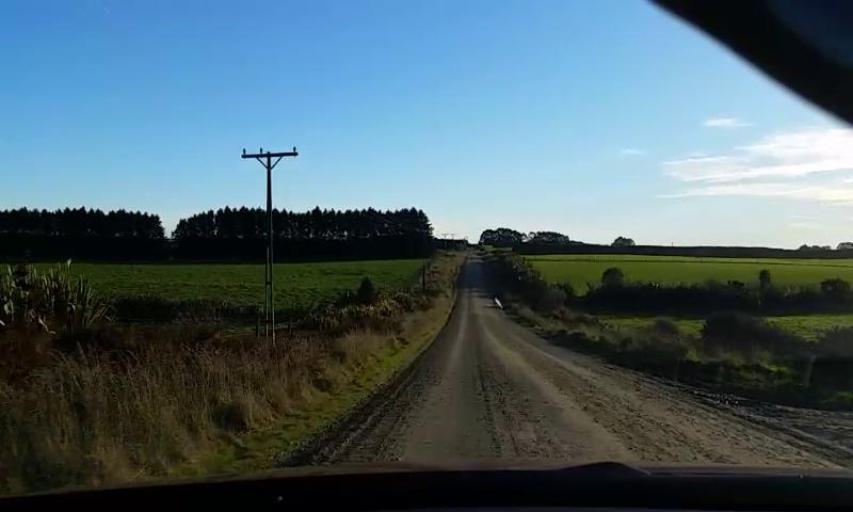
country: NZ
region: Southland
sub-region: Invercargill City
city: Invercargill
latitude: -46.2851
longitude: 168.4850
